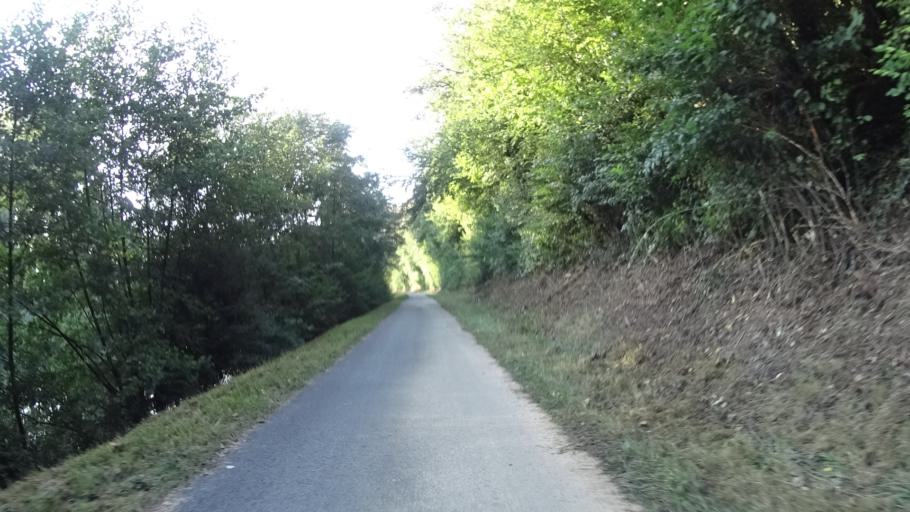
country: FR
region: Franche-Comte
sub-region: Territoire de Belfort
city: Mezire
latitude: 47.5429
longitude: 6.9068
